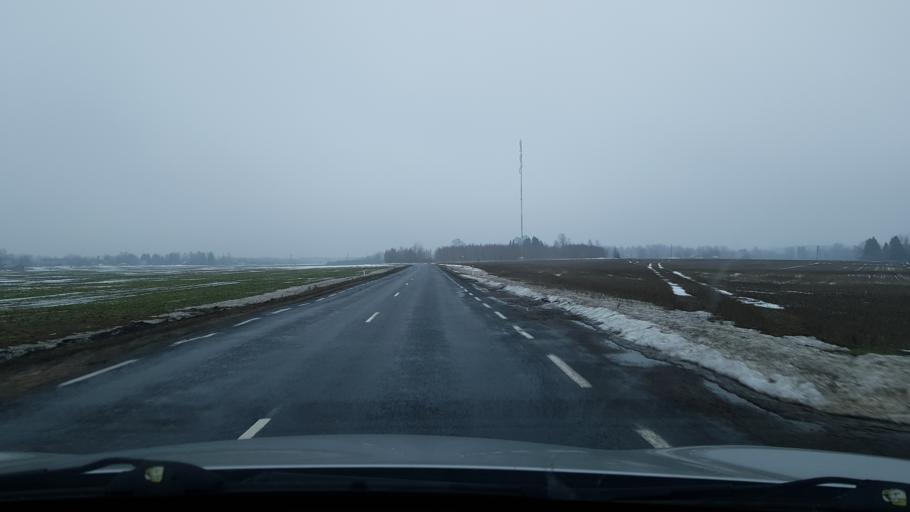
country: EE
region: Valgamaa
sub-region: Torva linn
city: Torva
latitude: 58.1579
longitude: 25.9630
